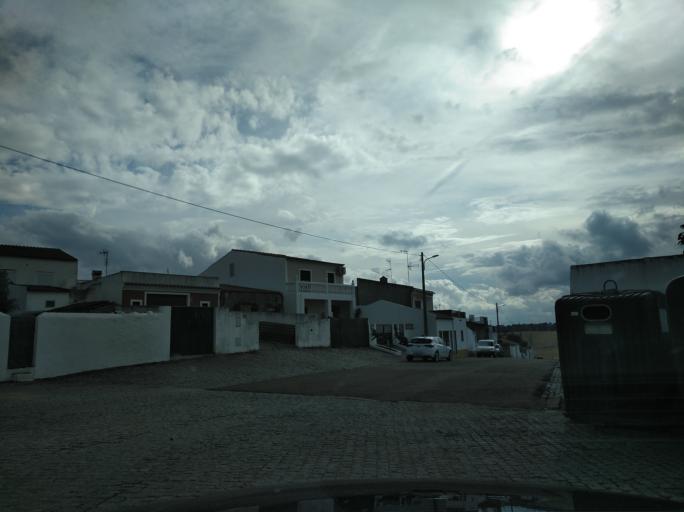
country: PT
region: Portalegre
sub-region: Campo Maior
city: Campo Maior
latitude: 39.0598
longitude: -7.1237
